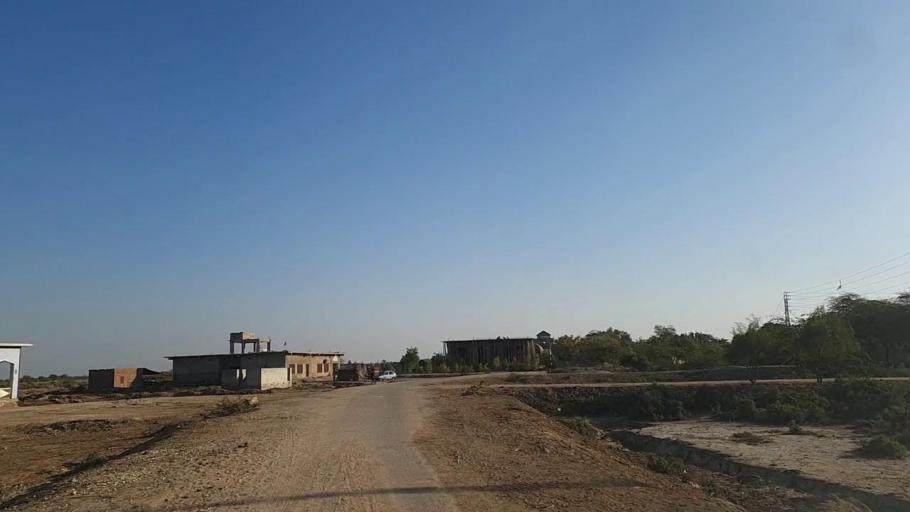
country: PK
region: Sindh
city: Samaro
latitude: 25.3403
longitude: 69.3986
